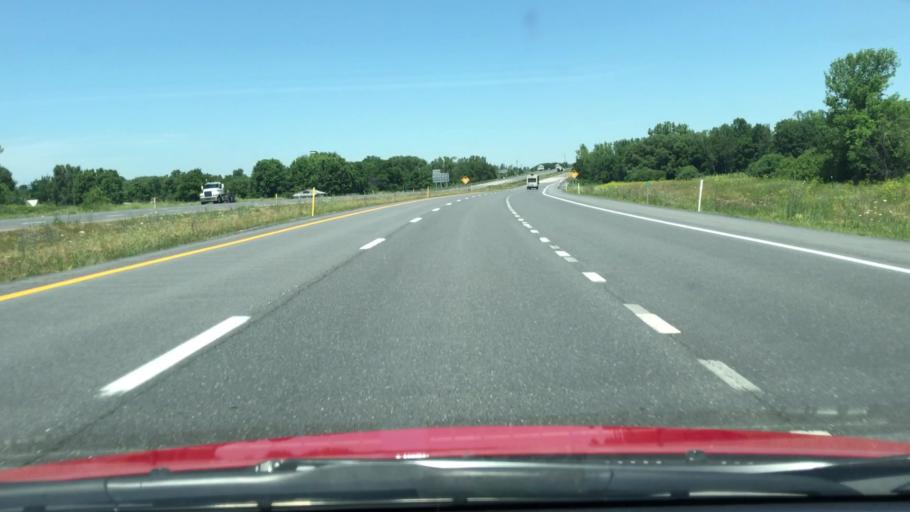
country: US
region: New York
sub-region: Clinton County
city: Champlain
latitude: 44.9838
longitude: -73.4576
